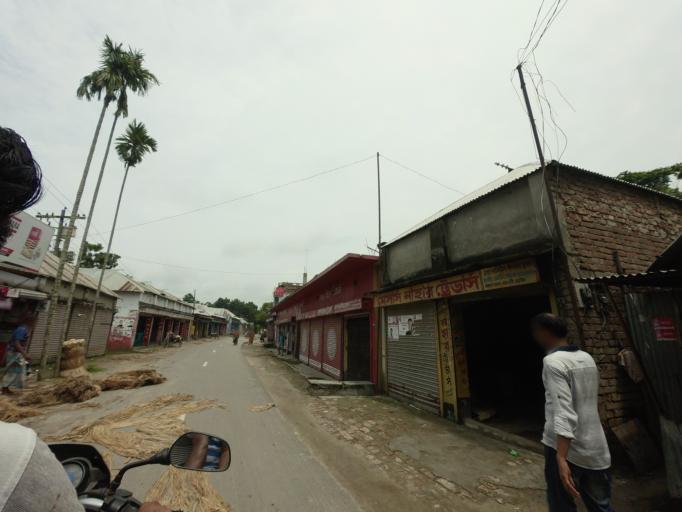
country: BD
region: Khulna
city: Kalia
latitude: 23.0859
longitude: 89.6697
